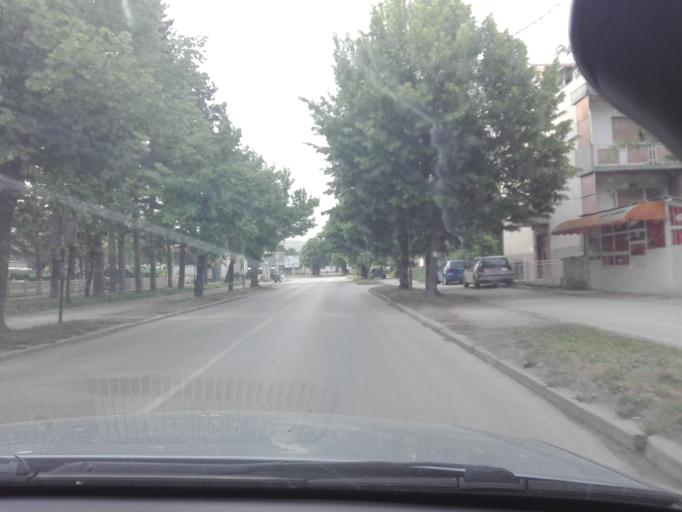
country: MK
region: Bitola
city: Bitola
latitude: 41.0224
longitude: 21.3398
